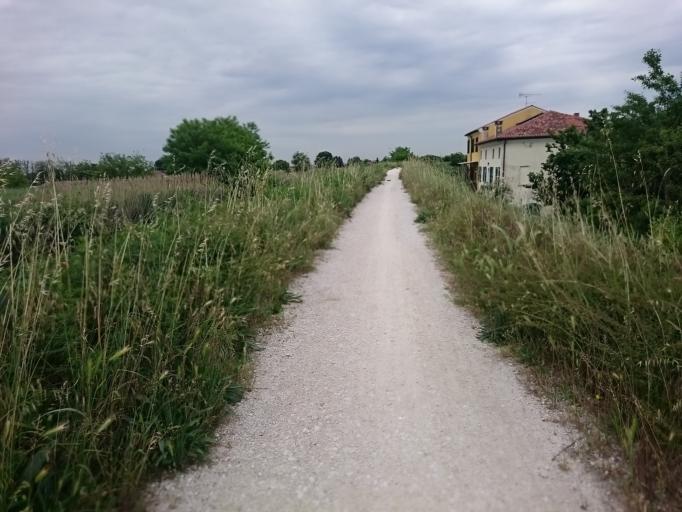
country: IT
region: Veneto
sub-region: Provincia di Padova
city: Baone
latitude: 45.2206
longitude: 11.7052
